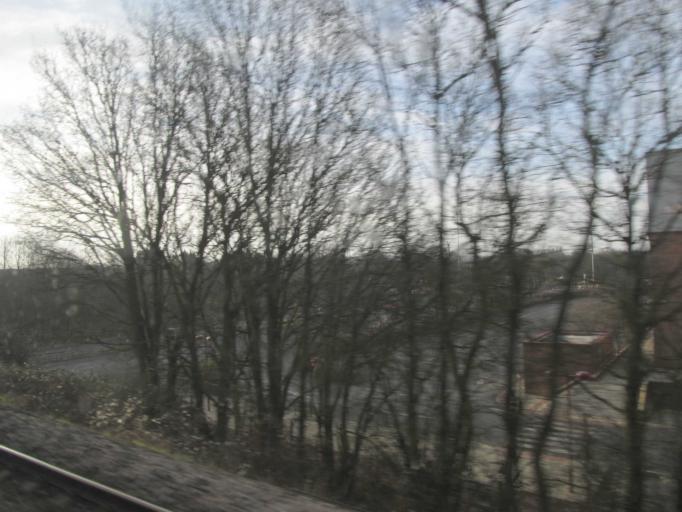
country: GB
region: England
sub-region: Wokingham
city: Woodley
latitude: 51.4386
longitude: -0.8982
